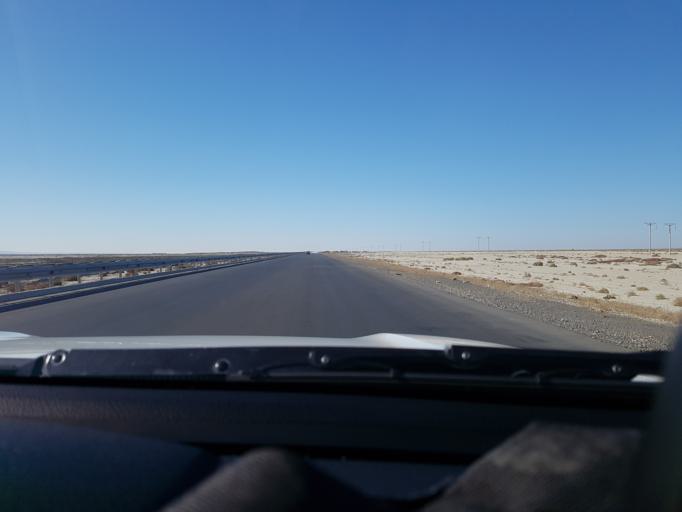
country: TM
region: Balkan
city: Gazanjyk
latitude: 39.2513
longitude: 55.1002
